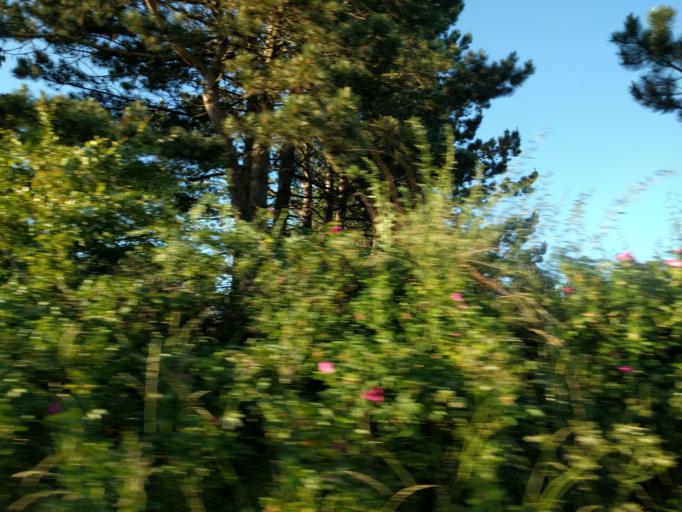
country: DK
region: South Denmark
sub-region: Kerteminde Kommune
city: Munkebo
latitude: 55.6065
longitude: 10.6224
